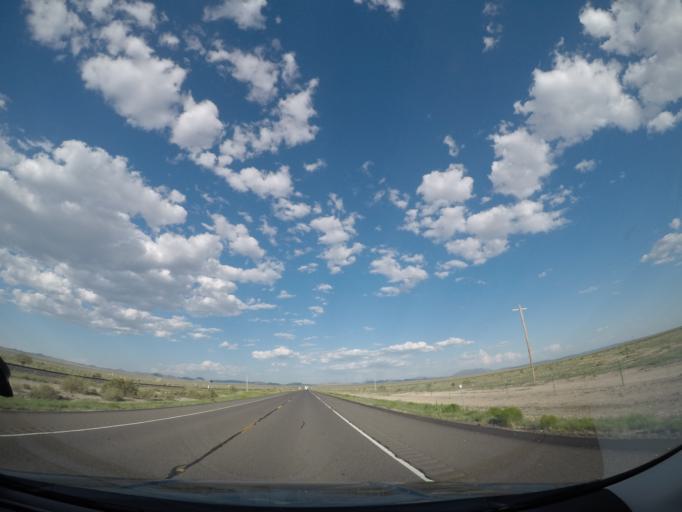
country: US
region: Texas
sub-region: Presidio County
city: Marfa
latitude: 30.2929
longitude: -103.9489
